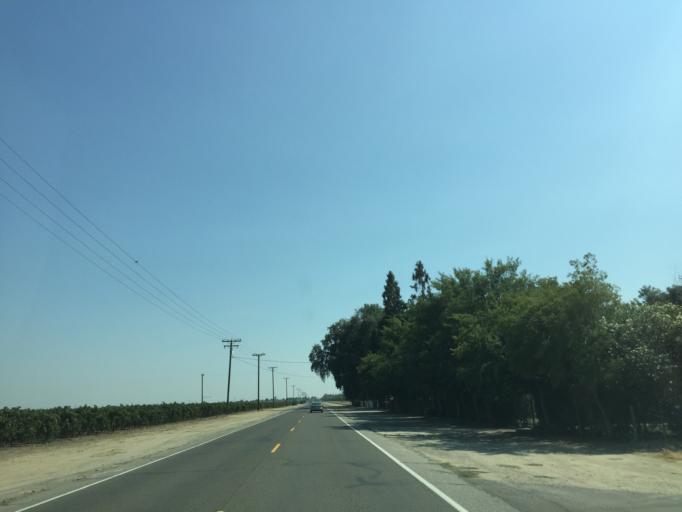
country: US
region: California
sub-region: Kings County
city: Lucerne
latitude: 36.3664
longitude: -119.6730
